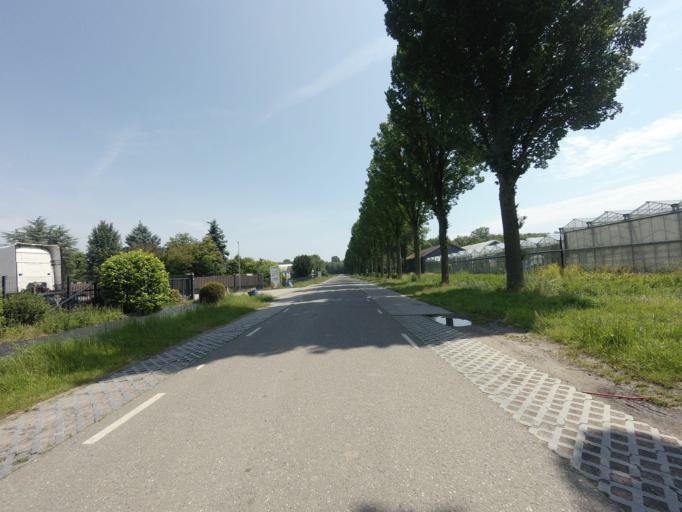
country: NL
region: North Holland
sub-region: Gemeente Enkhuizen
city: Enkhuizen
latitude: 52.7121
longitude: 5.2435
